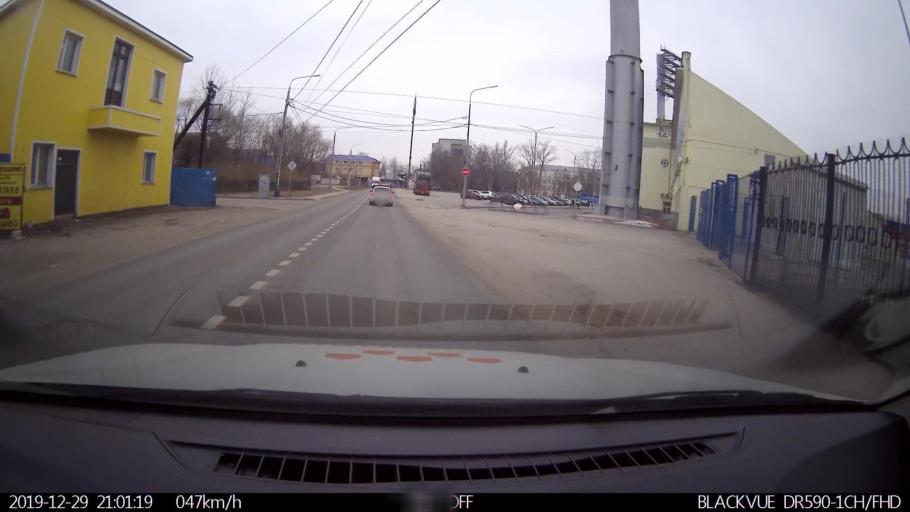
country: RU
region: Nizjnij Novgorod
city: Nizhniy Novgorod
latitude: 56.3085
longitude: 43.9280
